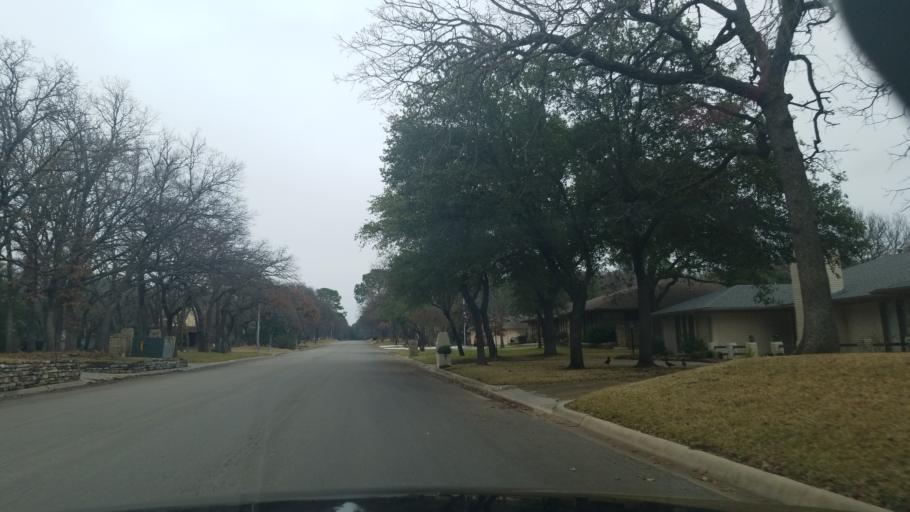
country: US
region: Texas
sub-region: Denton County
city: Denton
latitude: 33.1828
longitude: -97.1178
